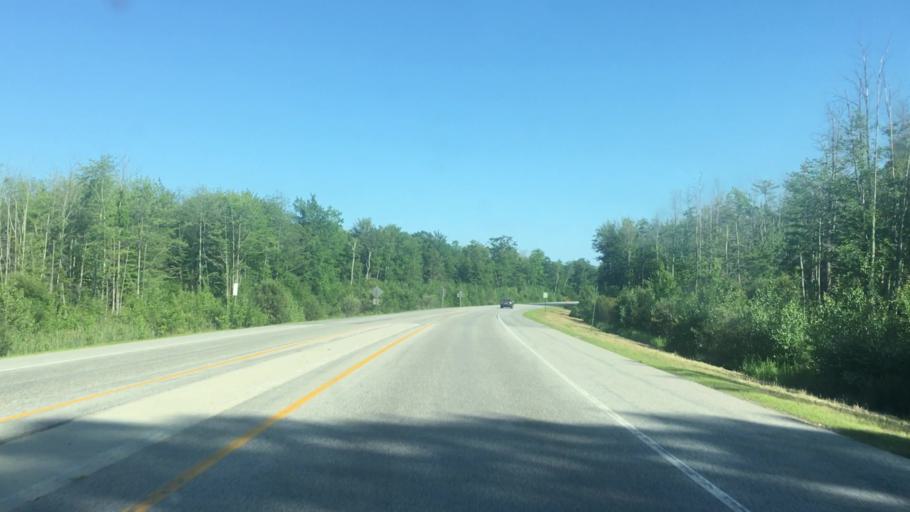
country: US
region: Maine
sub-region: Cumberland County
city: Gorham
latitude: 43.6683
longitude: -70.4558
